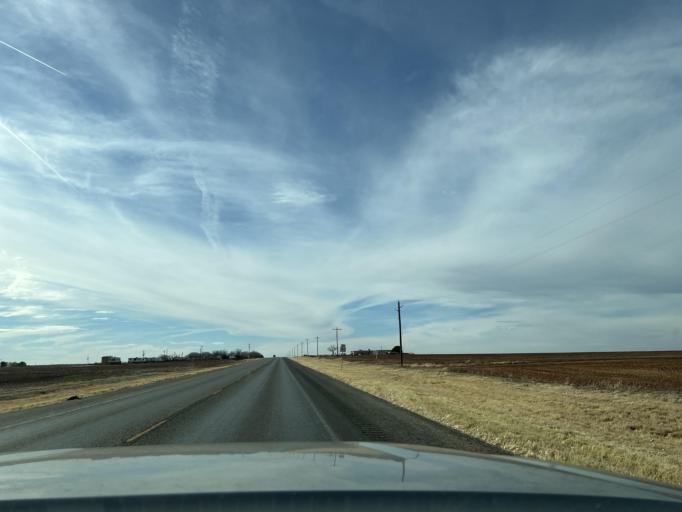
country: US
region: Texas
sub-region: Jones County
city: Anson
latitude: 32.7518
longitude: -99.9128
